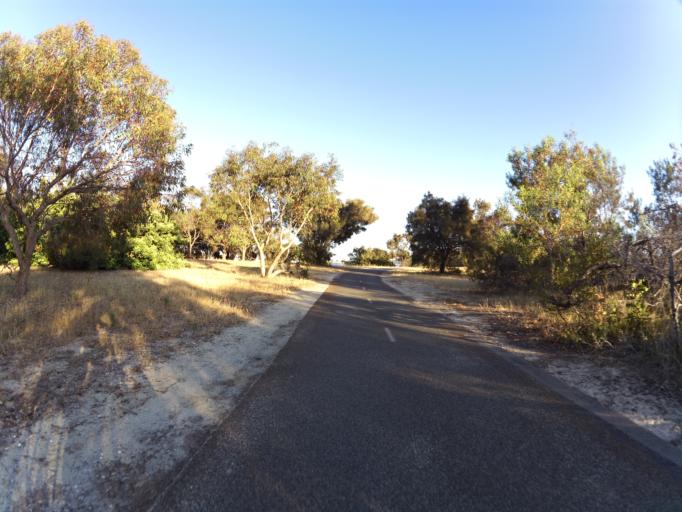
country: AU
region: Western Australia
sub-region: South Perth
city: Manning
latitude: -32.0086
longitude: 115.8549
